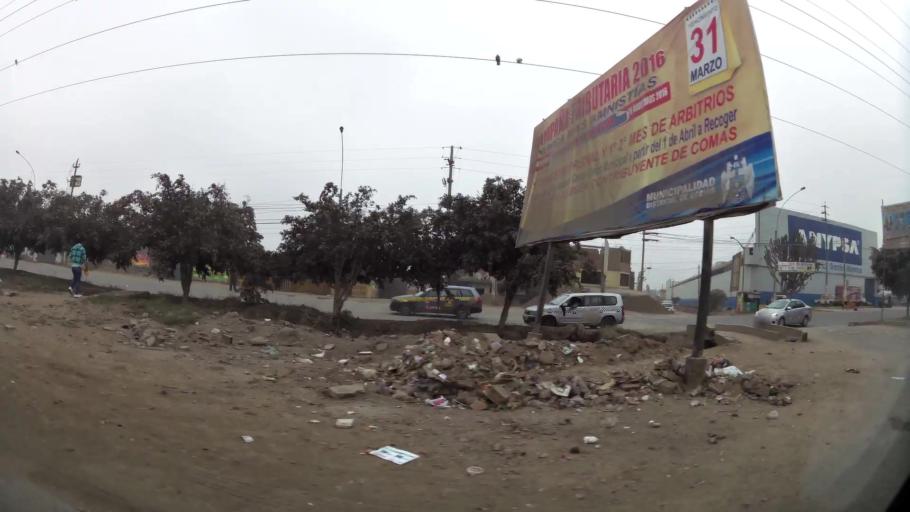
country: PE
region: Lima
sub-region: Lima
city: Urb. Santo Domingo
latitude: -11.8937
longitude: -77.0466
